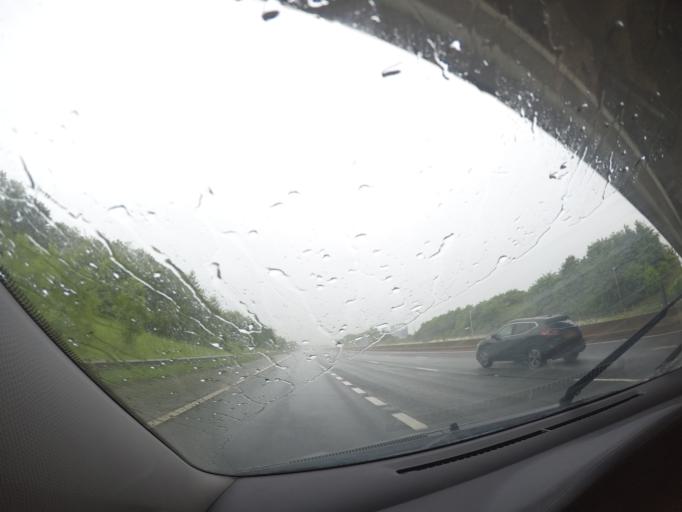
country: GB
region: England
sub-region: Cumbria
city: Penrith
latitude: 54.6559
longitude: -2.7653
